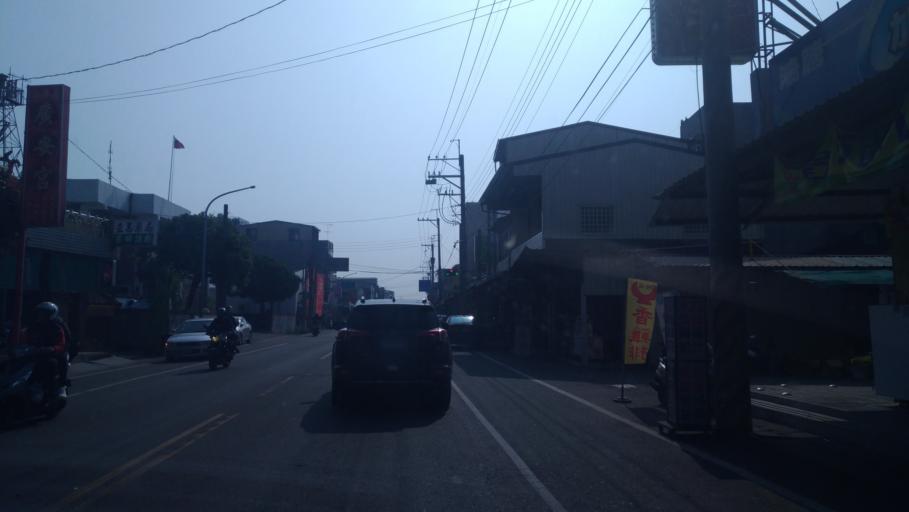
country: TW
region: Taiwan
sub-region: Chiayi
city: Jiayi Shi
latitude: 23.5262
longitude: 120.4202
